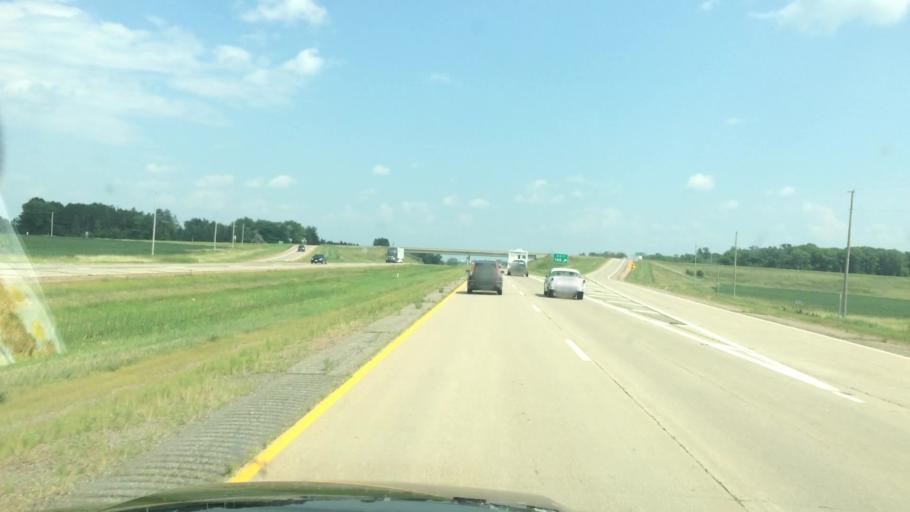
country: US
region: Wisconsin
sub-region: Marathon County
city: Athens
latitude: 44.9453
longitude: -90.0845
